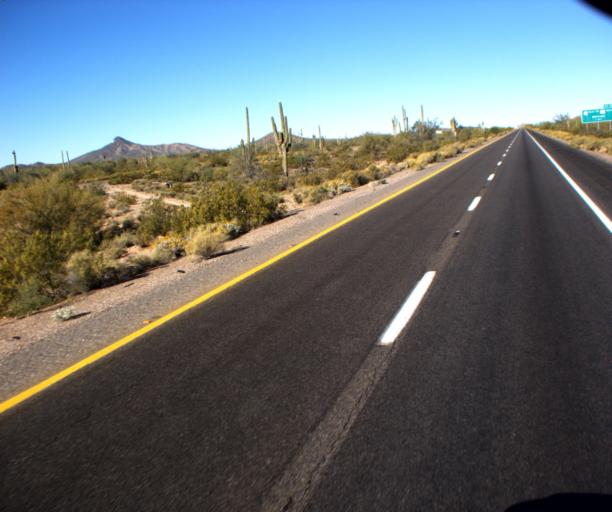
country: US
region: Arizona
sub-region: Pinal County
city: Maricopa
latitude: 32.8340
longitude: -112.1111
